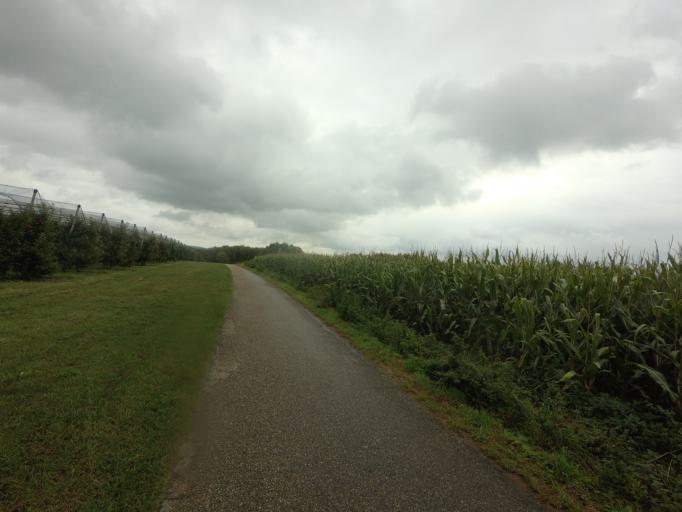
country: NL
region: Limburg
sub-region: Eijsden-Margraten
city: Margraten
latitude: 50.8024
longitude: 5.8594
